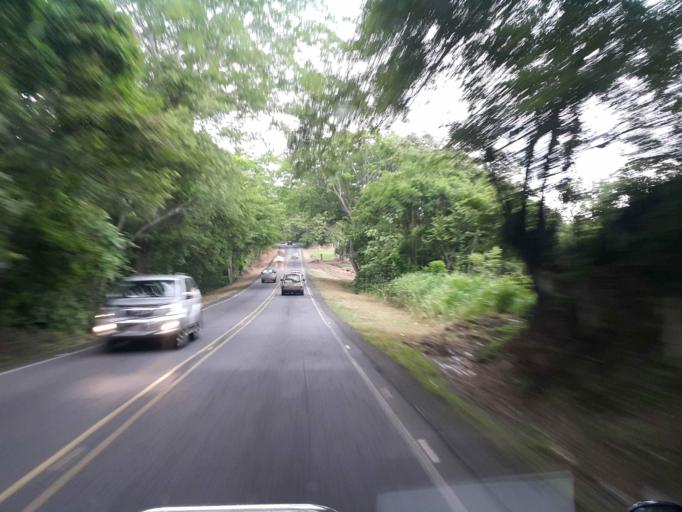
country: CR
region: Puntarenas
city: Miramar
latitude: 10.0878
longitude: -84.7923
